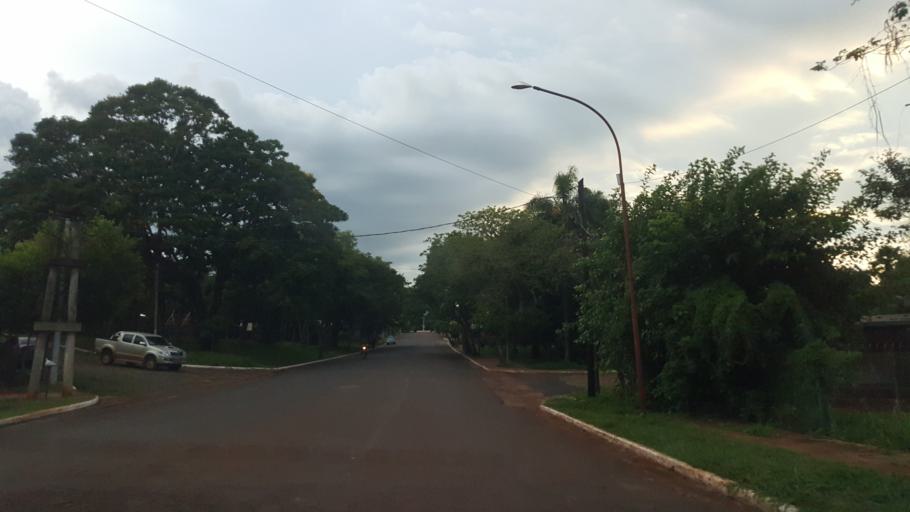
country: AR
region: Misiones
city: Jardin America
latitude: -27.0398
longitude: -55.2233
